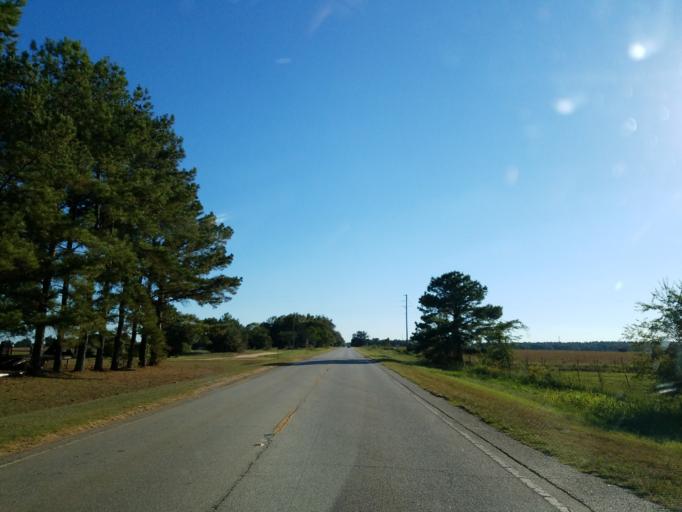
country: US
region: Georgia
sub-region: Lee County
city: Leesburg
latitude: 31.7621
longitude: -84.1490
